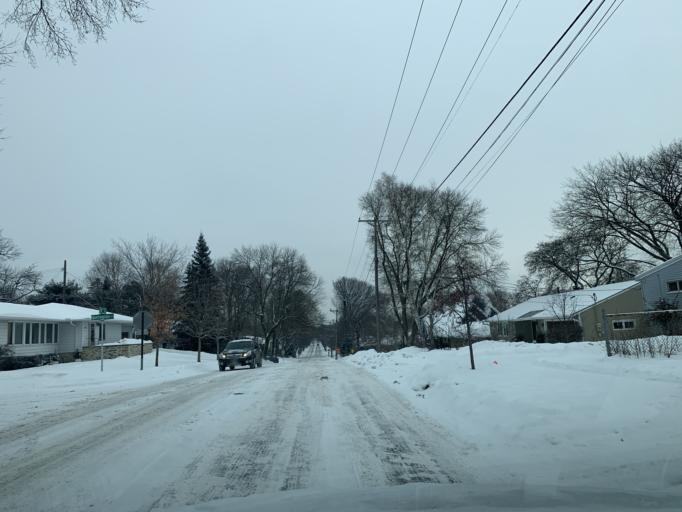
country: US
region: Minnesota
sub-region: Hennepin County
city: Saint Louis Park
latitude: 44.9324
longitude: -93.3318
